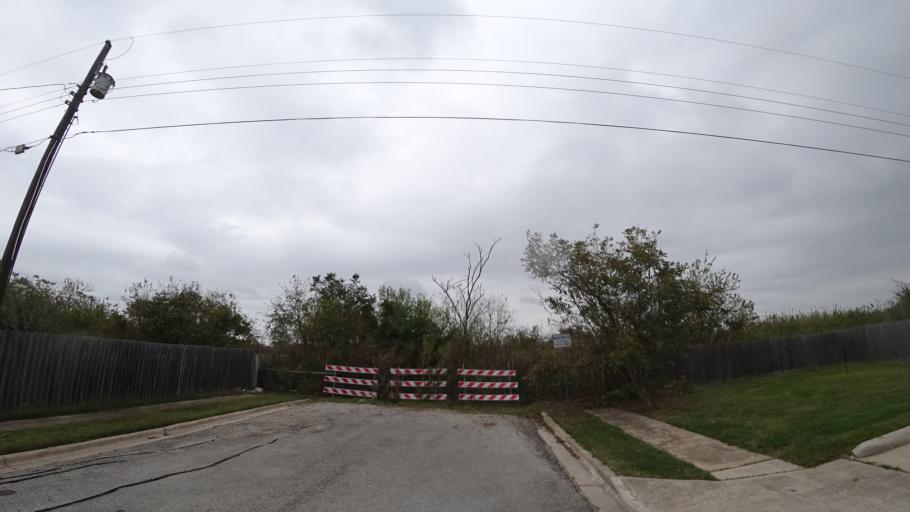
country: US
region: Texas
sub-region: Travis County
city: Pflugerville
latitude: 30.4249
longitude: -97.6085
